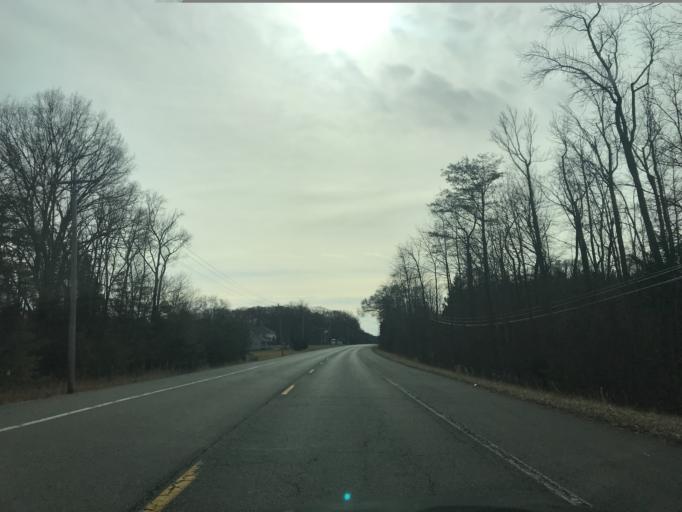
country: US
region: Virginia
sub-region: Prince William County
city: Quantico Station
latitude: 38.4631
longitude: -77.2185
